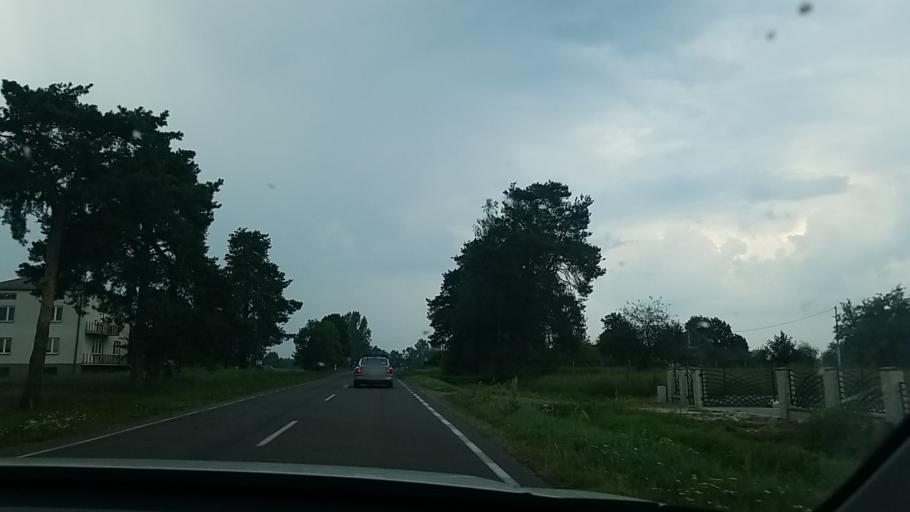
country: PL
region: Lublin Voivodeship
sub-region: Powiat leczynski
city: Cycow
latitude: 51.2717
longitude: 23.0962
